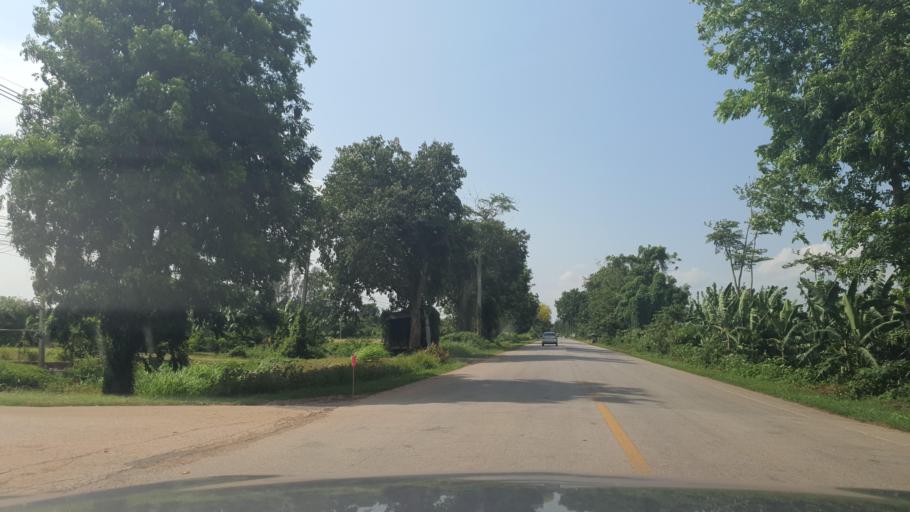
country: TH
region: Sukhothai
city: Si Samrong
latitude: 17.1822
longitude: 99.8518
